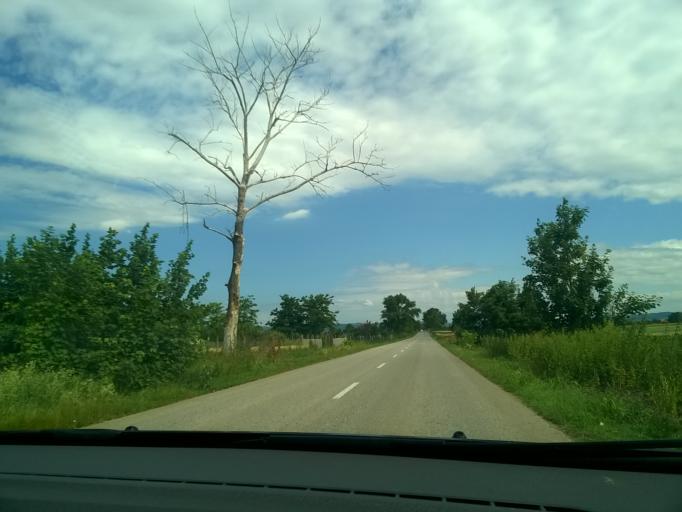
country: RS
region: Autonomna Pokrajina Vojvodina
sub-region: Sremski Okrug
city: Ruma
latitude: 45.0252
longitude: 19.8130
